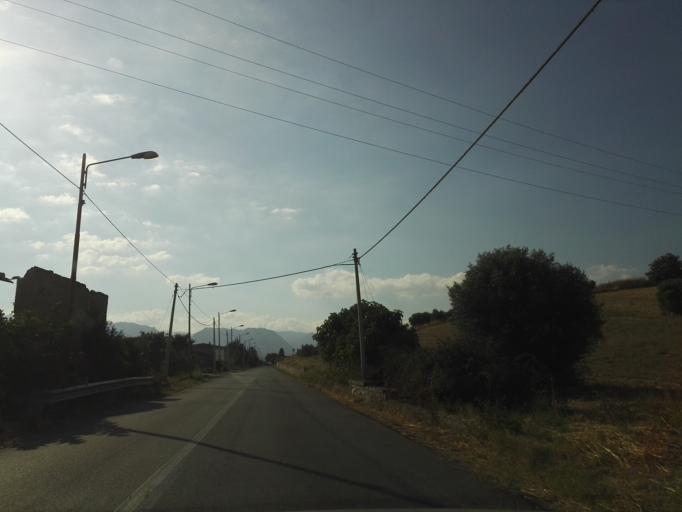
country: IT
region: Calabria
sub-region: Provincia di Reggio Calabria
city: Monasterace
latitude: 38.4425
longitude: 16.5417
